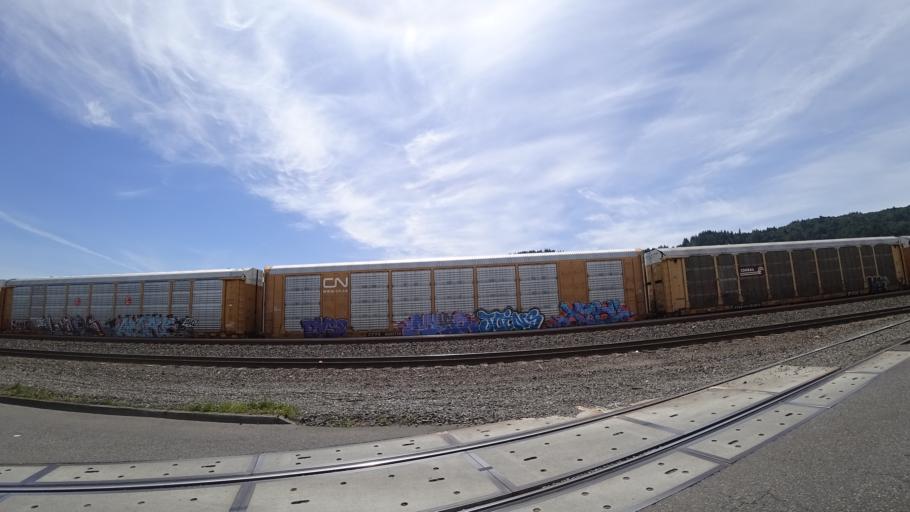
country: US
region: Oregon
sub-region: Multnomah County
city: Portland
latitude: 45.5535
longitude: -122.7193
